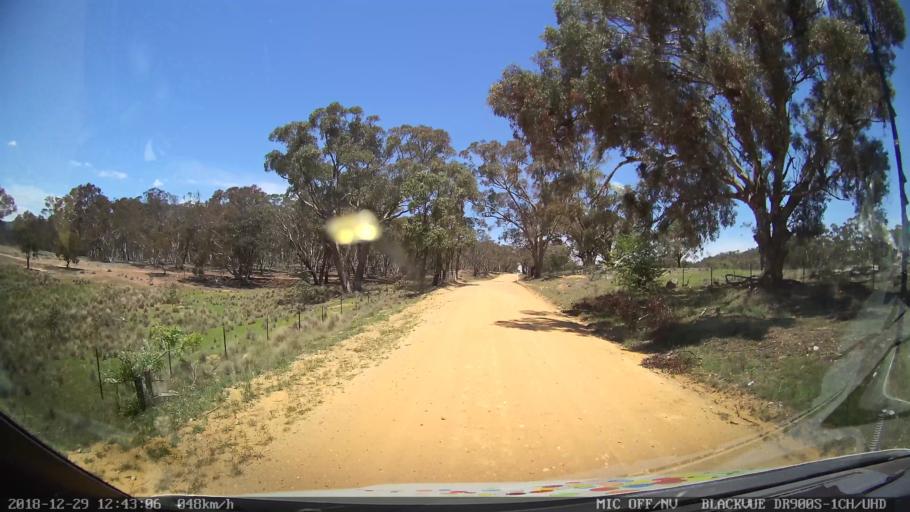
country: AU
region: Australian Capital Territory
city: Macarthur
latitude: -35.6178
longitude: 149.2184
